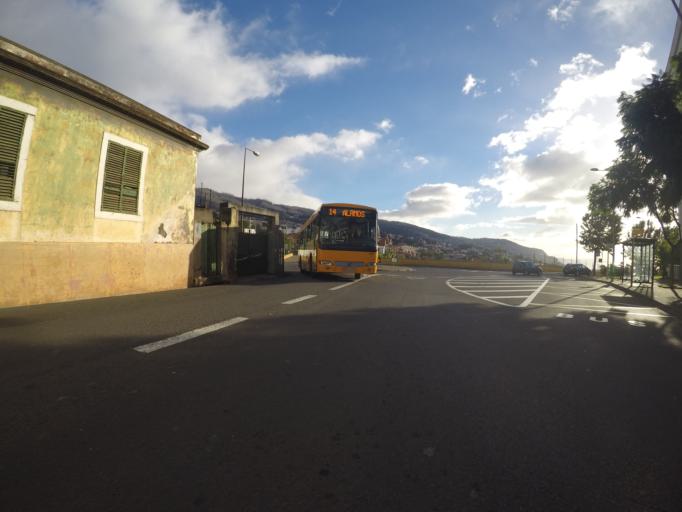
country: PT
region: Madeira
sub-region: Funchal
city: Nossa Senhora do Monte
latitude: 32.6650
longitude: -16.9367
